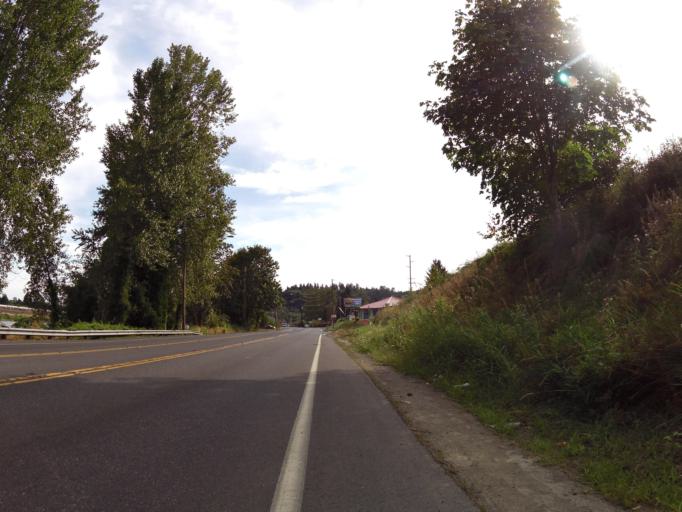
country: US
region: Washington
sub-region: Cowlitz County
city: West Side Highway
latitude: 46.1675
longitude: -122.9156
